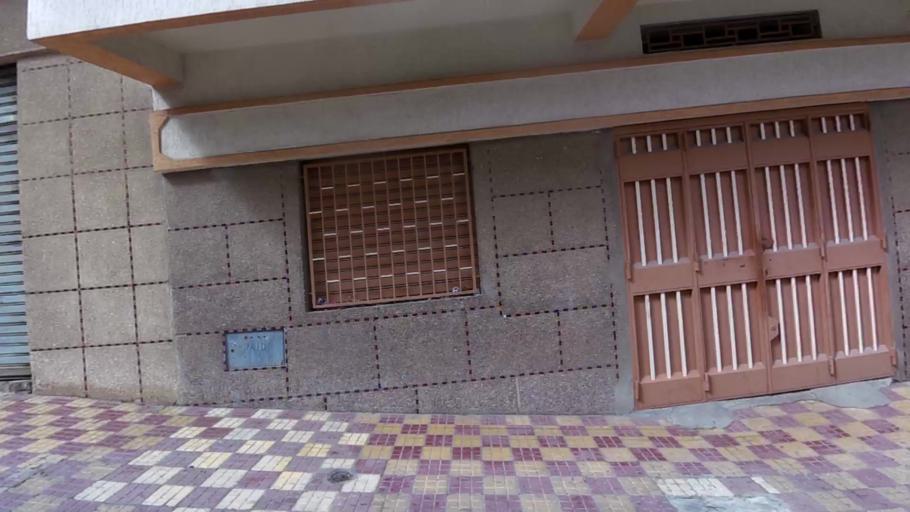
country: MA
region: Tanger-Tetouan
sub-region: Tanger-Assilah
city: Tangier
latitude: 35.7545
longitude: -5.8027
